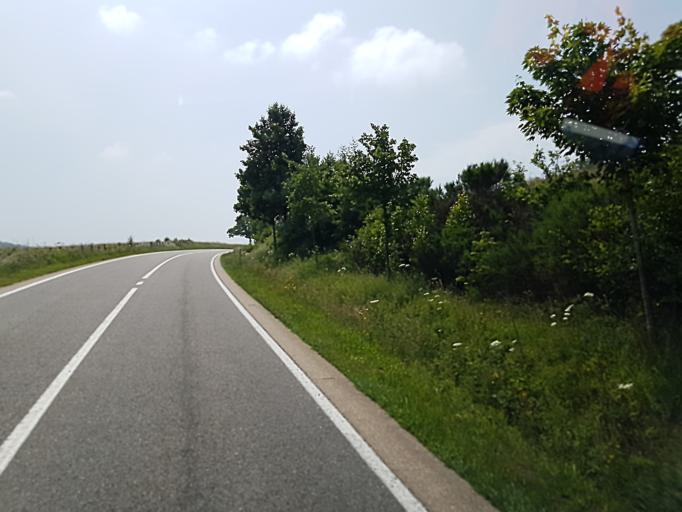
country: BE
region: Wallonia
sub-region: Province de Liege
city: Trois-Ponts
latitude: 50.3513
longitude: 5.8218
